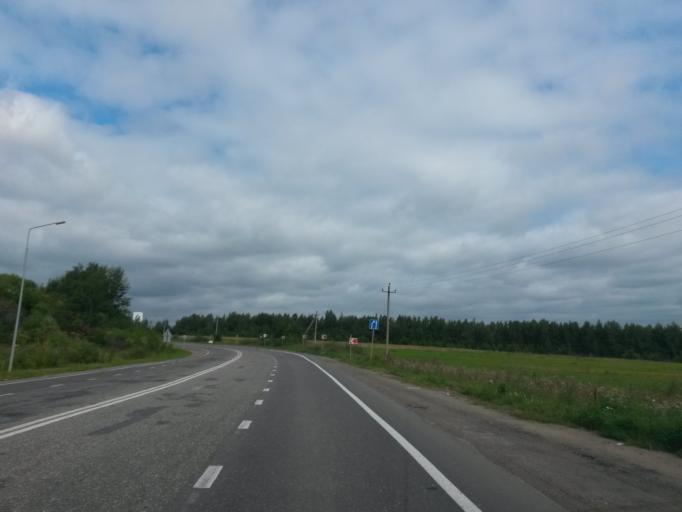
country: RU
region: Jaroslavl
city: Yaroslavl
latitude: 57.5546
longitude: 39.8611
